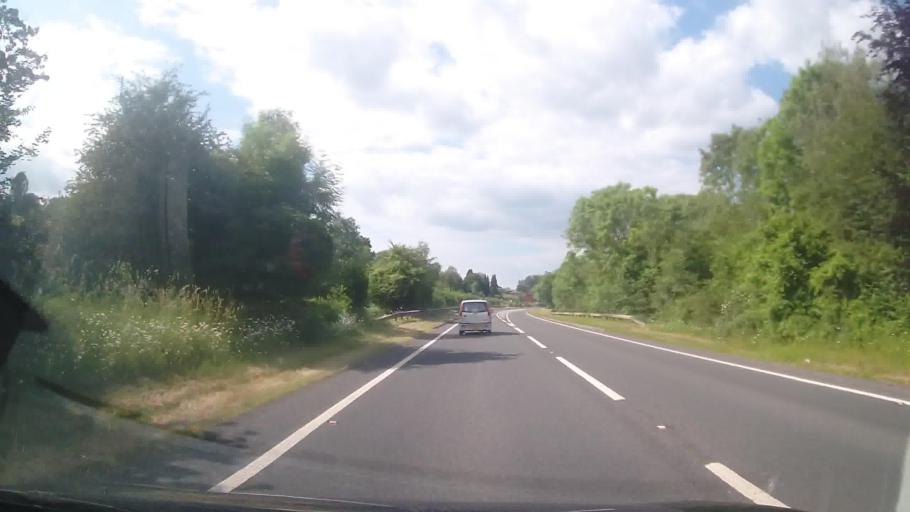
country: GB
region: England
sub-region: Herefordshire
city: Hope under Dinmore
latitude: 52.1894
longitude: -2.7175
